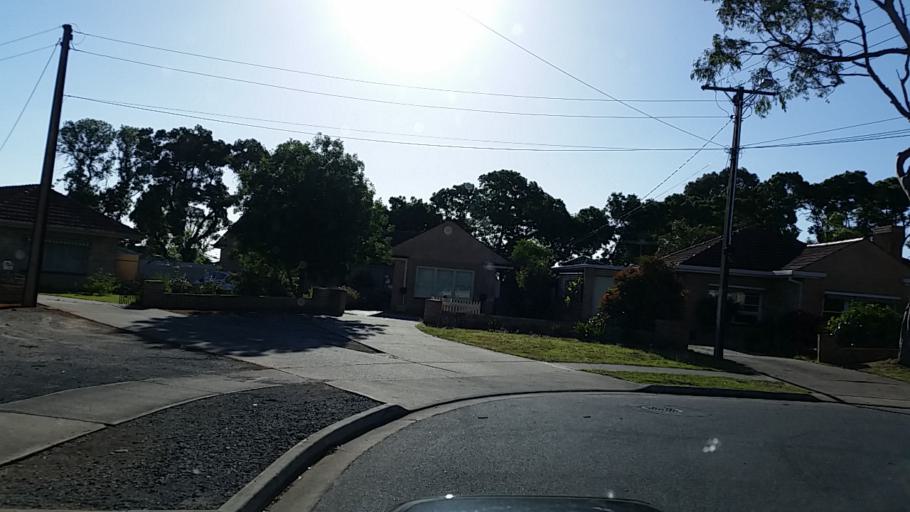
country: AU
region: South Australia
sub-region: Marion
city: South Plympton
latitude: -34.9785
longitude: 138.5594
